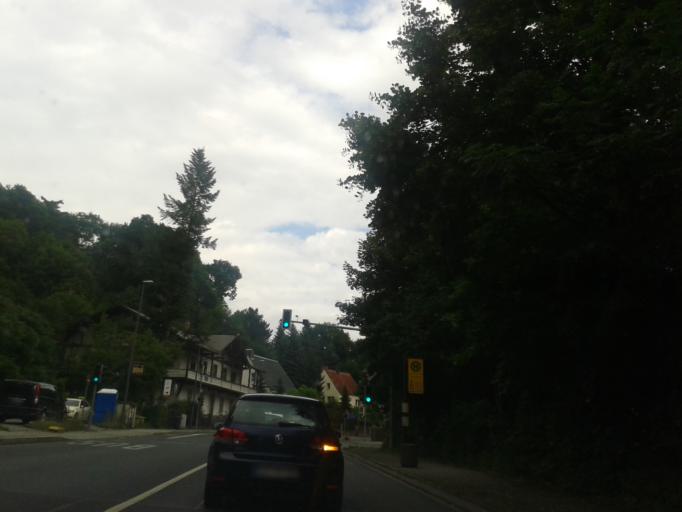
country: DE
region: Saxony
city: Albertstadt
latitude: 51.0592
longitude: 13.8322
